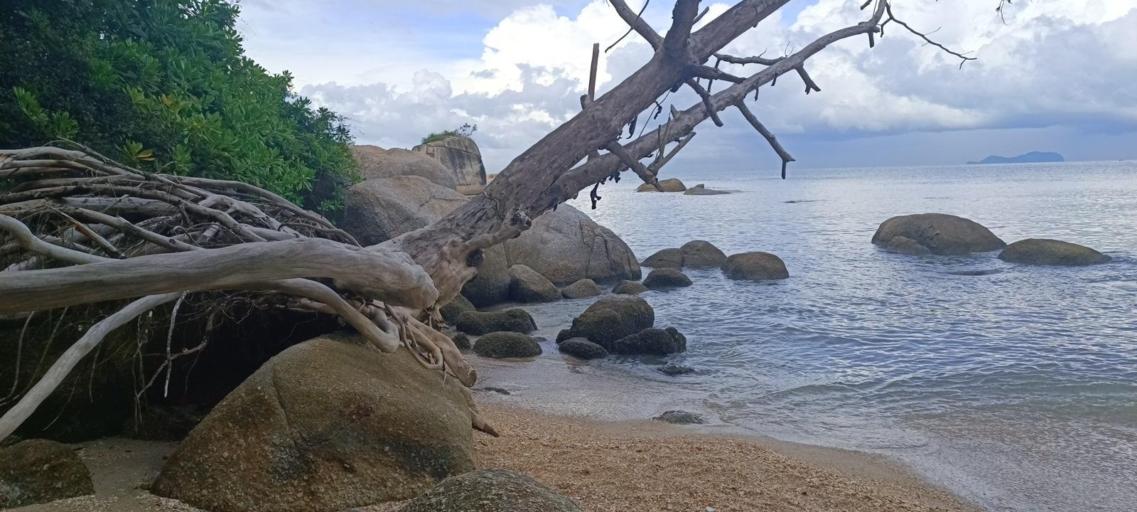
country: MY
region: Penang
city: Kampung Sungai Ara
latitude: 5.2655
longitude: 100.2727
